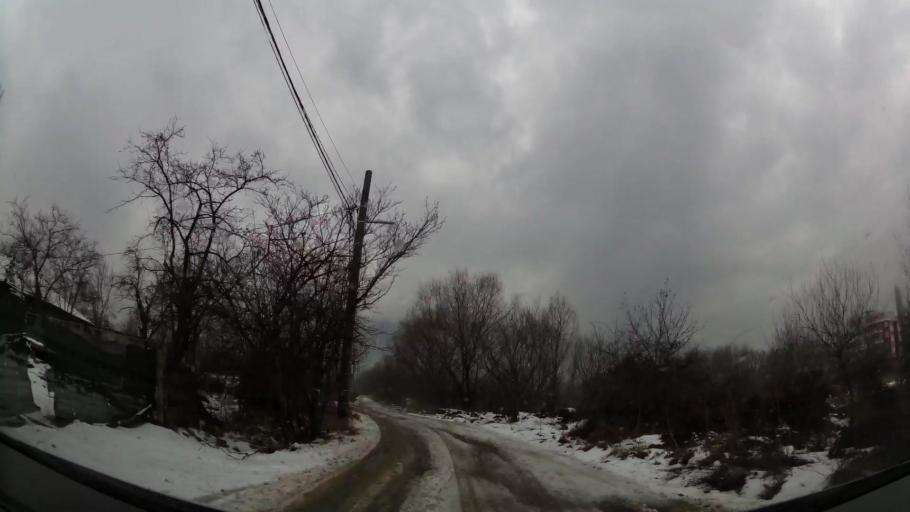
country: BG
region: Sofia-Capital
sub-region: Stolichna Obshtina
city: Sofia
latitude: 42.6555
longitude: 23.3001
